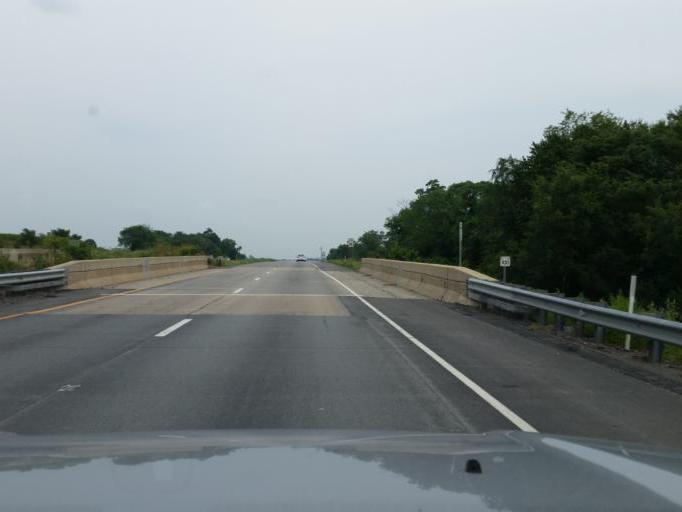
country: US
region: Pennsylvania
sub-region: Lancaster County
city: Rheems
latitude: 40.1399
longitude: -76.5512
